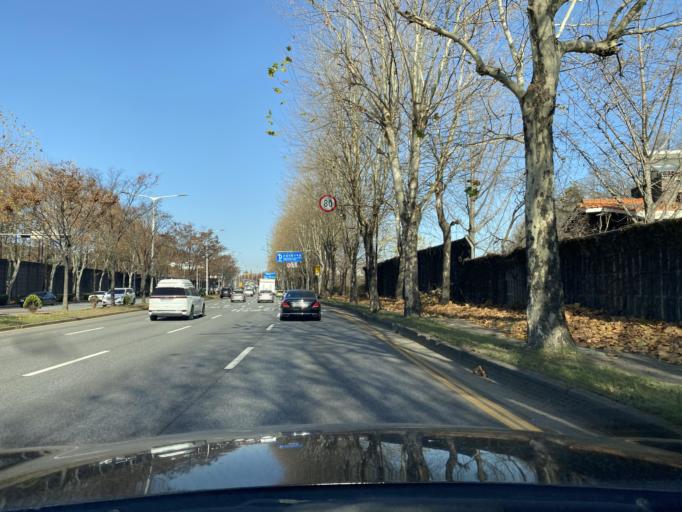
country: KR
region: Incheon
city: Incheon
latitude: 37.4423
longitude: 126.7428
